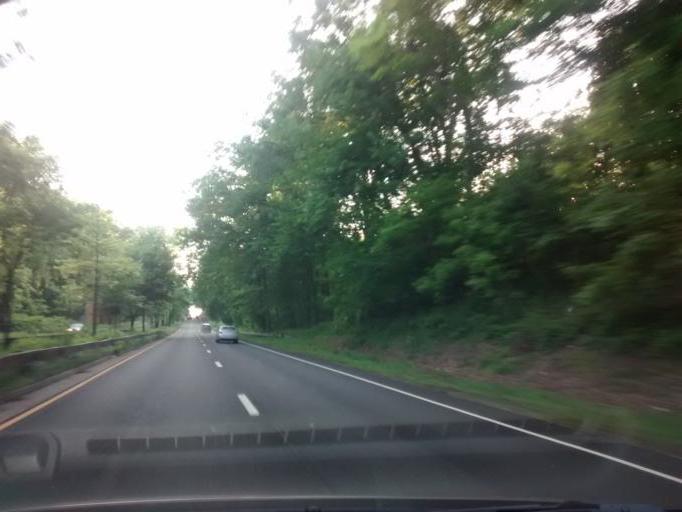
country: US
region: Connecticut
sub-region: Fairfield County
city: Glenville
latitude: 41.0973
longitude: -73.6409
